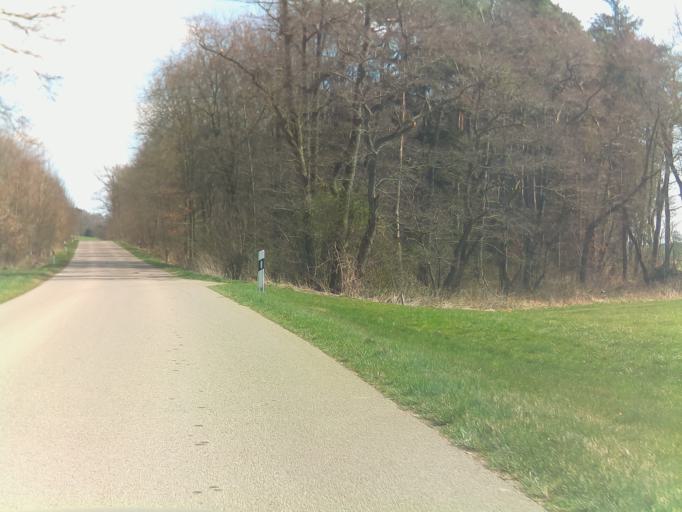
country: DE
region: Bavaria
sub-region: Swabia
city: Todtenweis
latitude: 48.5344
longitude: 10.9321
